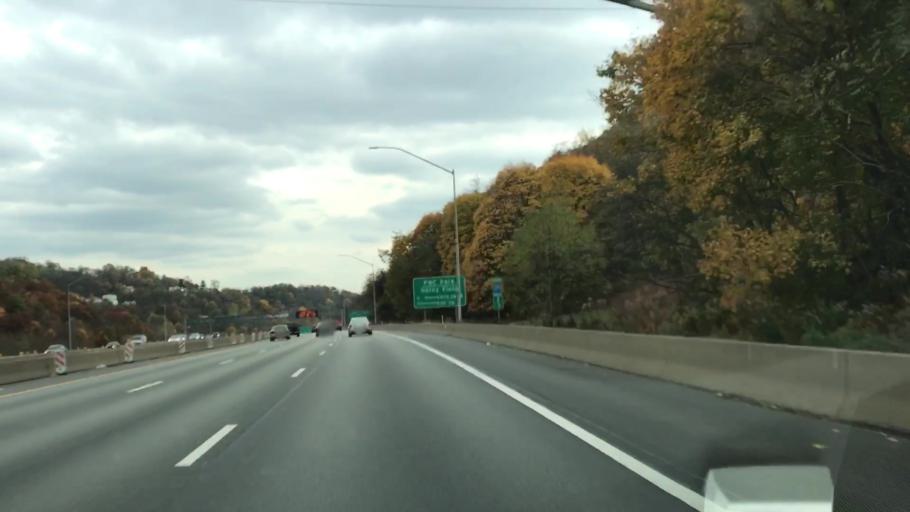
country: US
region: Pennsylvania
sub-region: Allegheny County
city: Millvale
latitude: 40.4729
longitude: -80.0055
